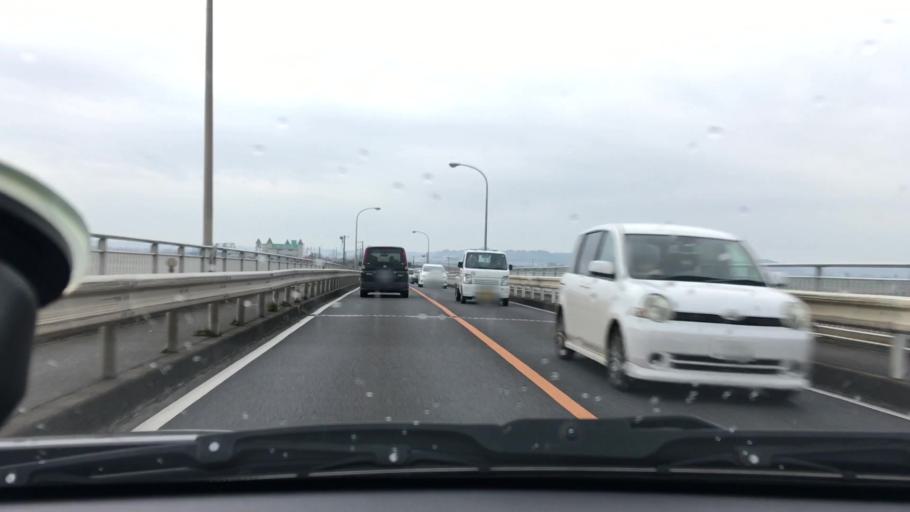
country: JP
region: Chiba
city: Omigawa
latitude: 35.8732
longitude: 140.6232
